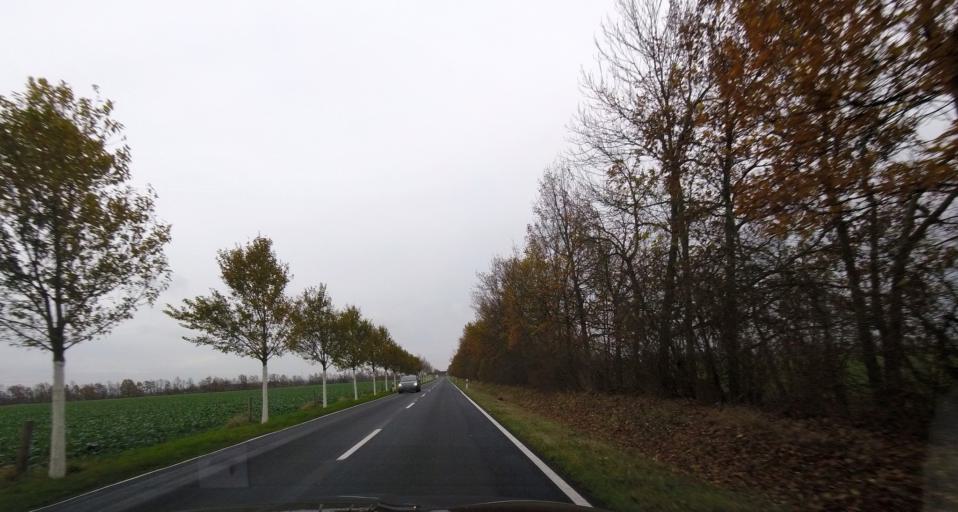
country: DE
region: Brandenburg
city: Niemegk
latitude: 52.0333
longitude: 12.7296
